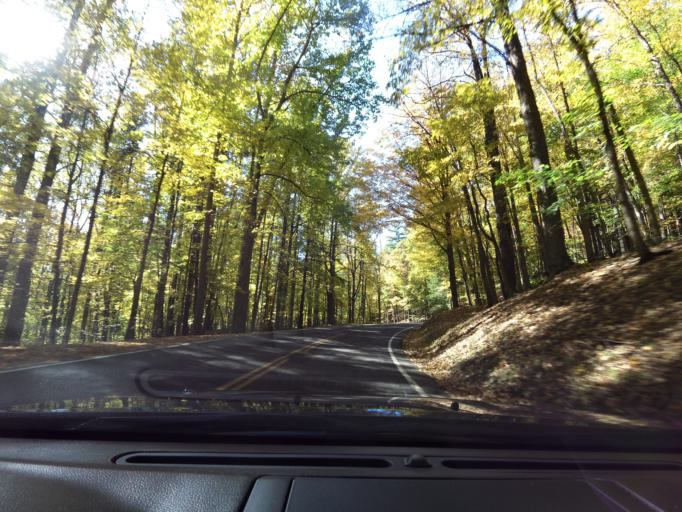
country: US
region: New York
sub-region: Wyoming County
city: Castile
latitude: 42.5831
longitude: -78.0468
